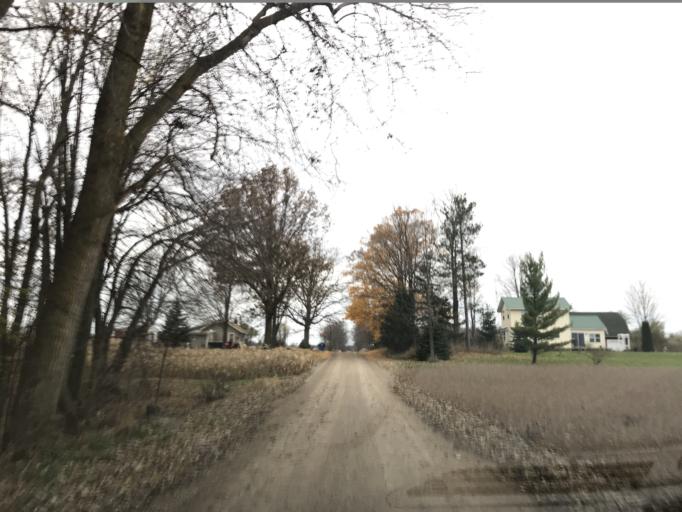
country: US
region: Michigan
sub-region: Lenawee County
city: Manitou Beach-Devils Lake
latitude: 42.0121
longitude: -84.3350
